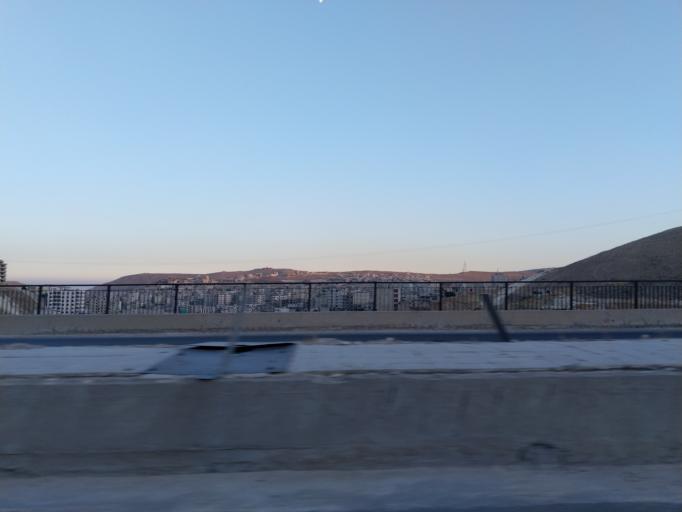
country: SY
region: Rif-dimashq
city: At Tall
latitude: 33.5852
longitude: 36.2914
